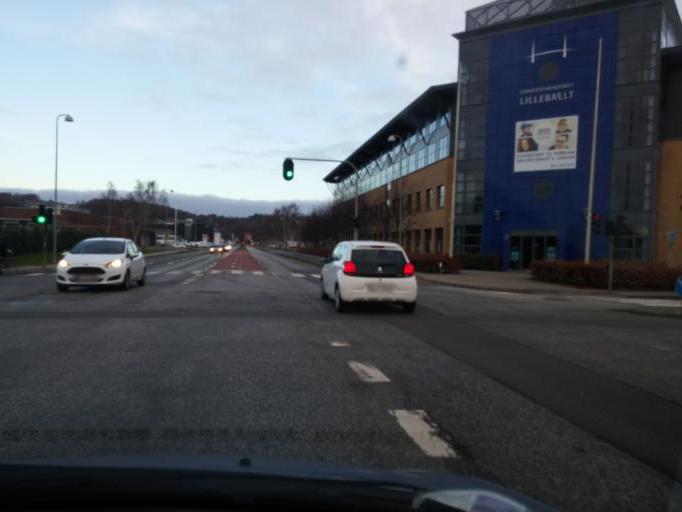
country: DK
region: South Denmark
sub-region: Vejle Kommune
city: Vejle
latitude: 55.7065
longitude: 9.5225
